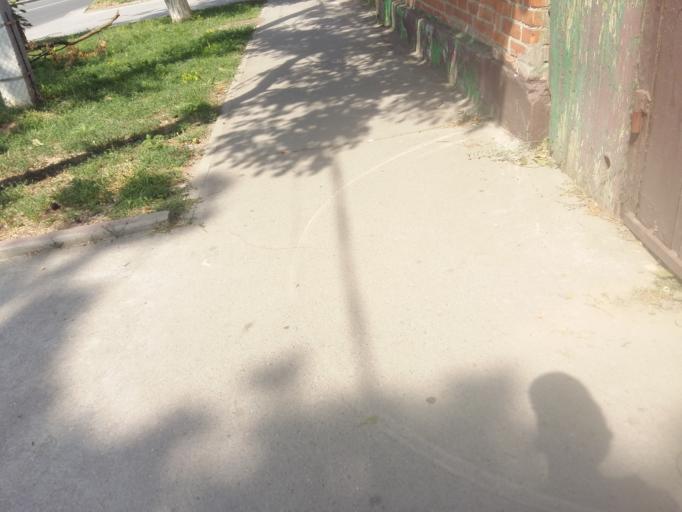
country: RU
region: Rostov
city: Imeni Chkalova
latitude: 47.2798
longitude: 39.7512
